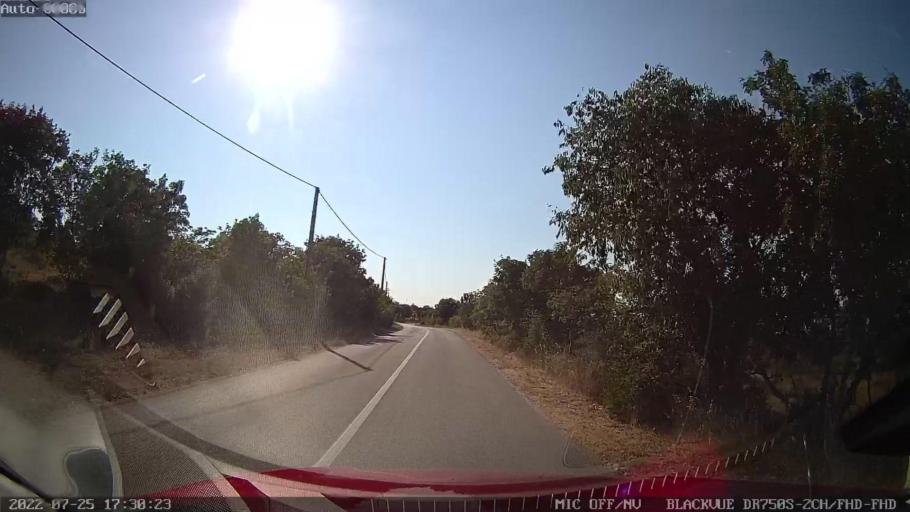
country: HR
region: Zadarska
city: Pridraga
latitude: 44.1644
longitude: 15.5093
